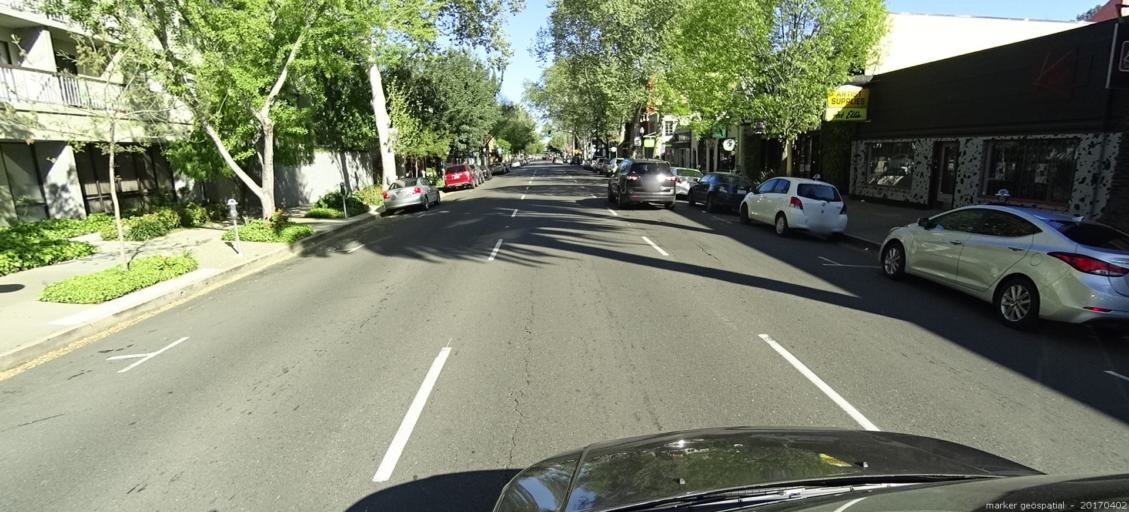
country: US
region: California
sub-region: Sacramento County
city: Sacramento
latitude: 38.5749
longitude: -121.4731
